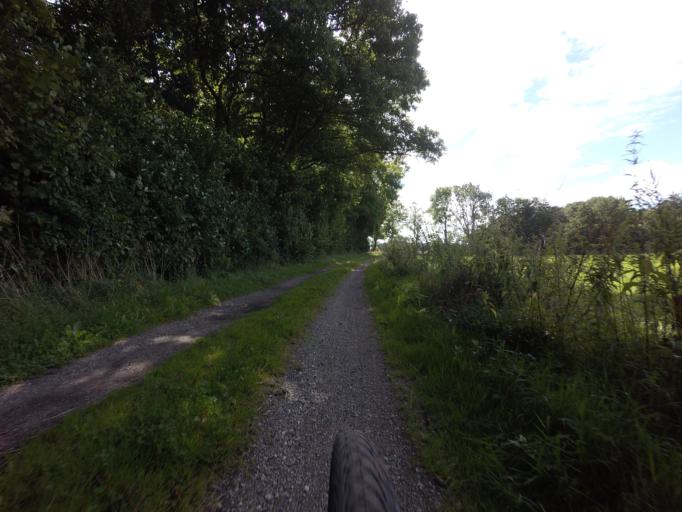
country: DK
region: Central Jutland
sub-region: Norddjurs Kommune
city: Allingabro
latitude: 56.4390
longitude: 10.3489
